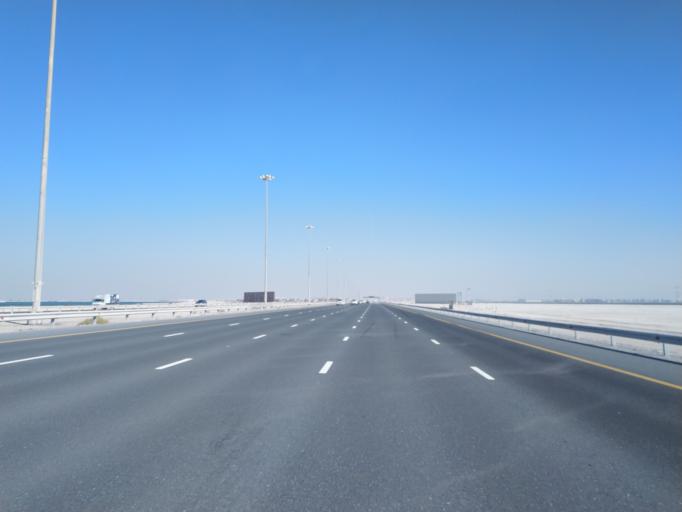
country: AE
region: Abu Dhabi
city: Abu Dhabi
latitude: 24.5123
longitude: 54.5444
